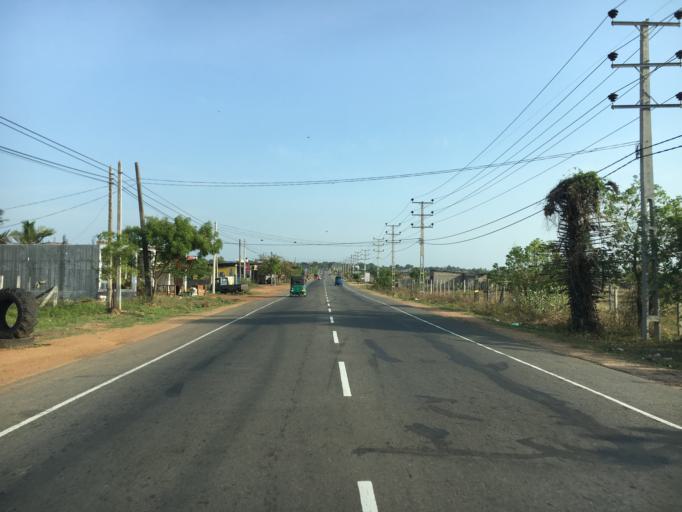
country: LK
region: Eastern Province
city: Eravur Town
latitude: 7.9332
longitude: 81.5111
